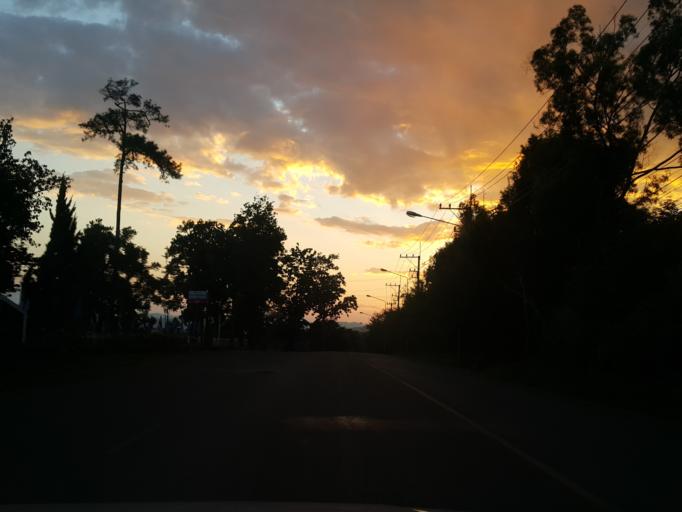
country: TH
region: Mae Hong Son
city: Khun Yuam
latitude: 18.8402
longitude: 97.9513
